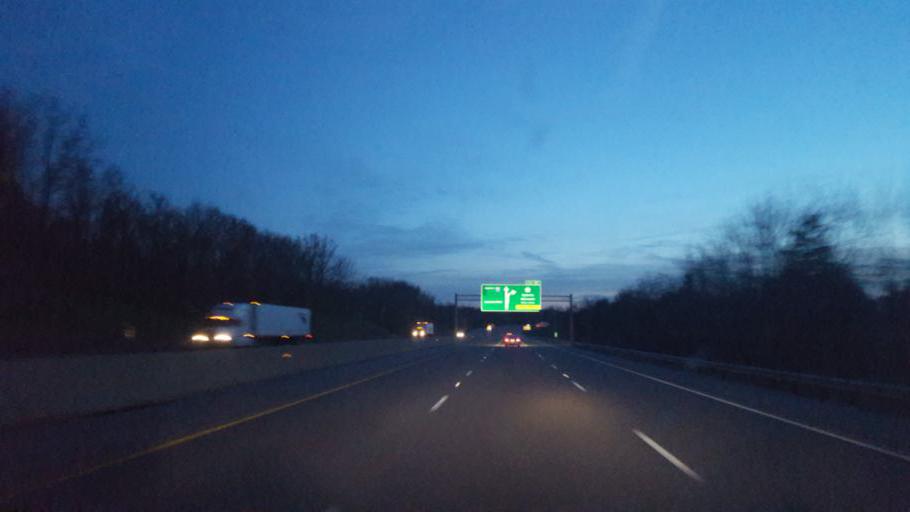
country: US
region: Kentucky
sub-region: Gallatin County
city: Warsaw
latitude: 38.7190
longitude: -84.8697
